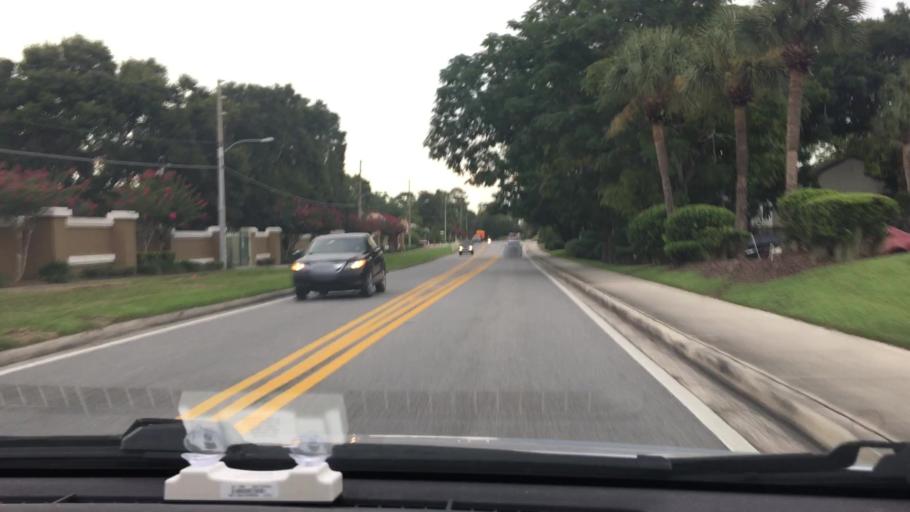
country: US
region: Florida
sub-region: Seminole County
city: Altamonte Springs
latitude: 28.6490
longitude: -81.3903
